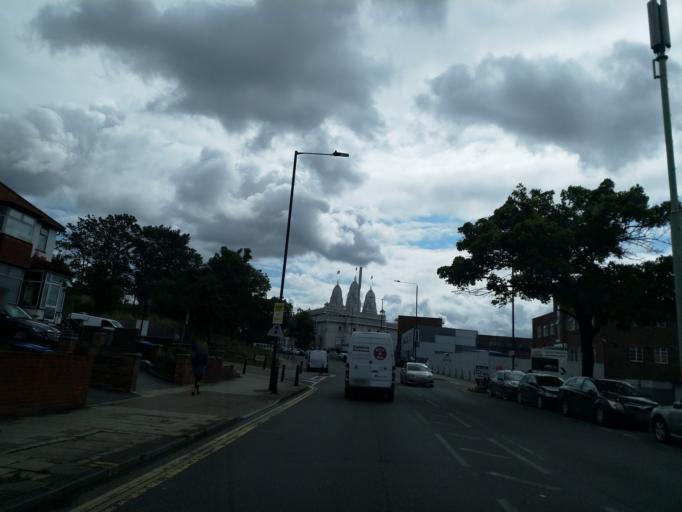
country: GB
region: England
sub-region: Greater London
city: Edgware
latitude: 51.5826
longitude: -0.2601
